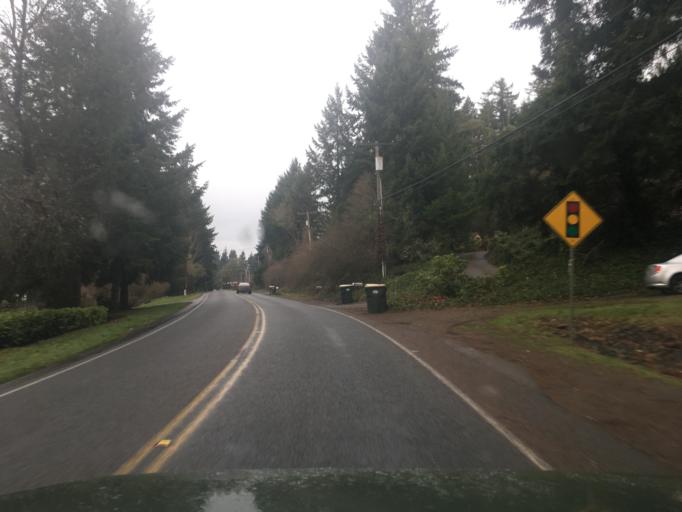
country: US
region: Washington
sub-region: Thurston County
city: Tanglewilde-Thompson Place
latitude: 47.0394
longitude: -122.7806
